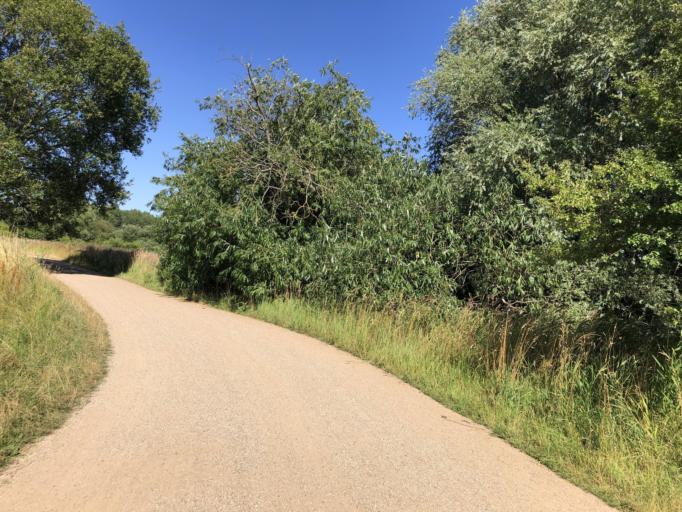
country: DK
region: Capital Region
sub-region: Kobenhavn
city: Copenhagen
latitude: 55.6558
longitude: 12.5733
